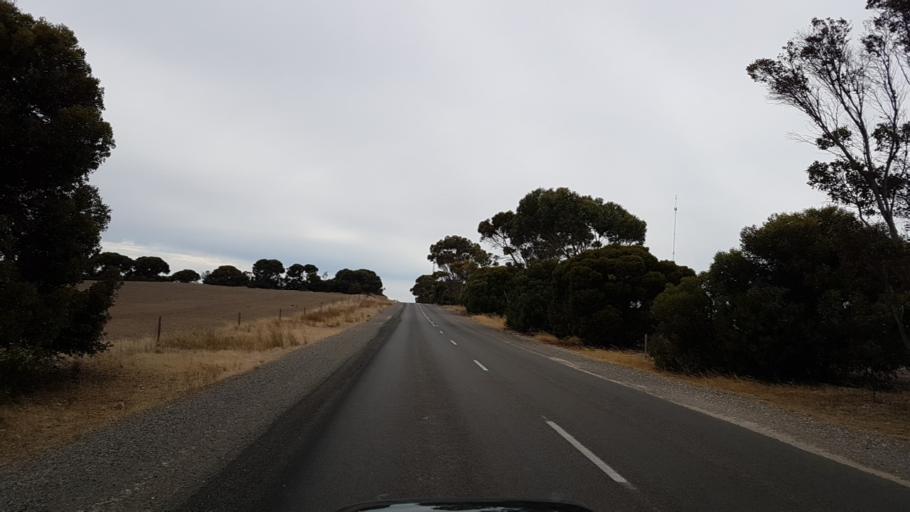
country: AU
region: South Australia
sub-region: Yorke Peninsula
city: Honiton
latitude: -34.9850
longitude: 137.2586
